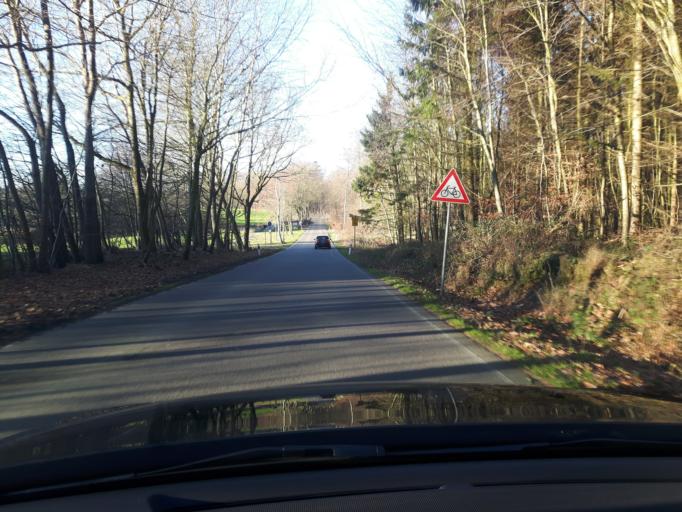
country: DE
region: Mecklenburg-Vorpommern
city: Sehlen
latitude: 54.3809
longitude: 13.4218
